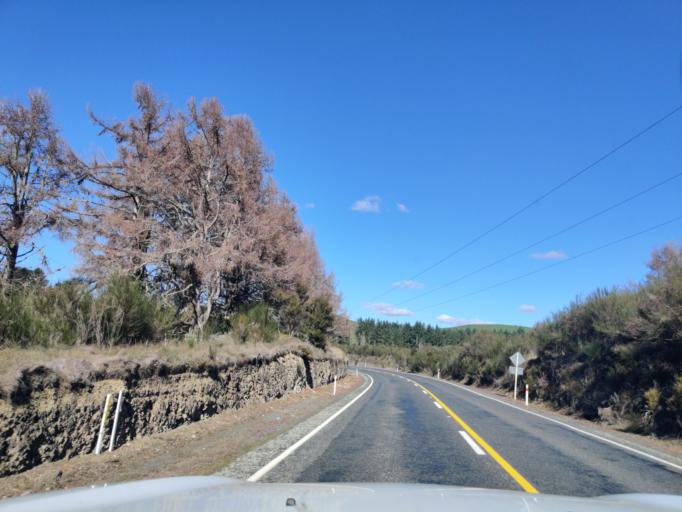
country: NZ
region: Waikato
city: Turangi
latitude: -38.8481
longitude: 175.6833
